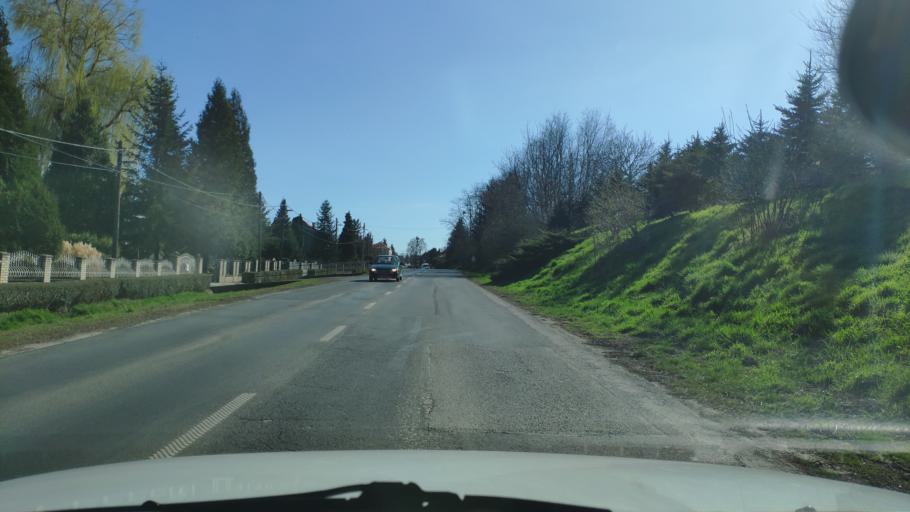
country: HU
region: Zala
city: Nagykanizsa
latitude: 46.4143
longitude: 16.9847
